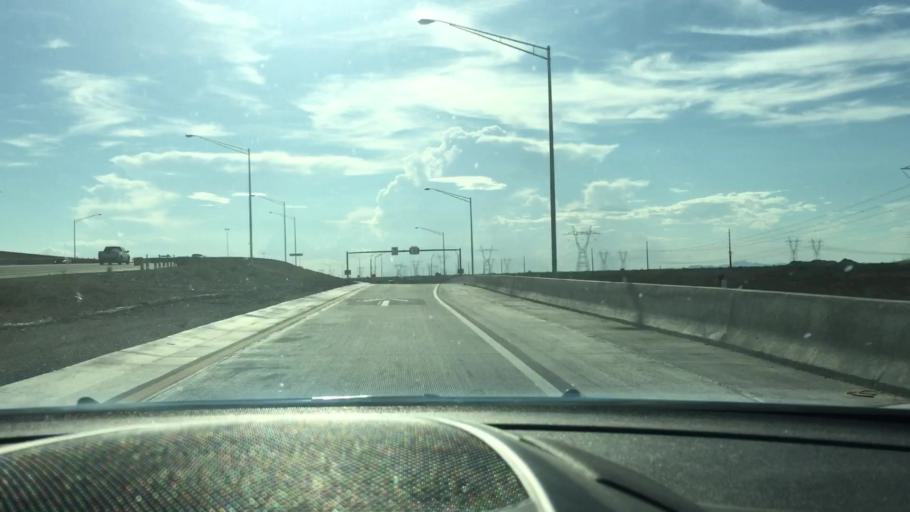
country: US
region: Arizona
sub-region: Maricopa County
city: Sun City West
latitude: 33.6988
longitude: -112.3310
